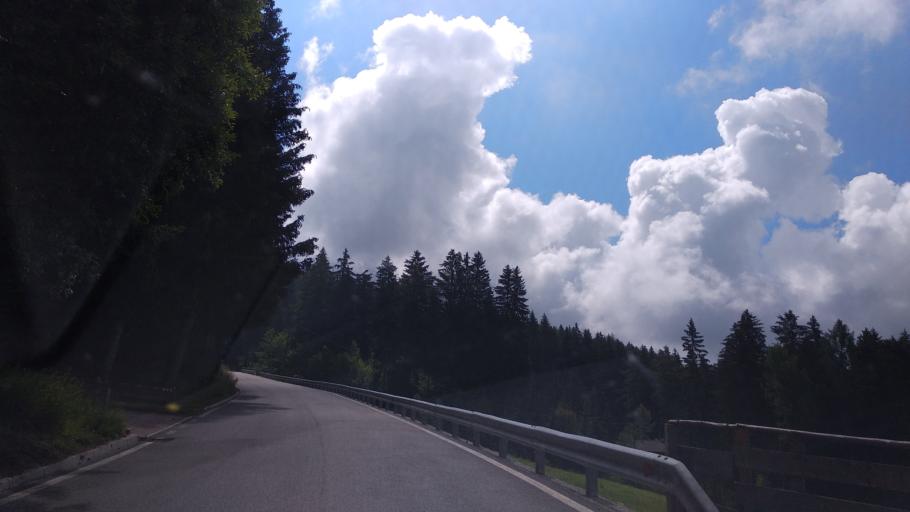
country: IT
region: Trentino-Alto Adige
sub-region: Bolzano
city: Avelengo
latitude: 46.6589
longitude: 11.2255
